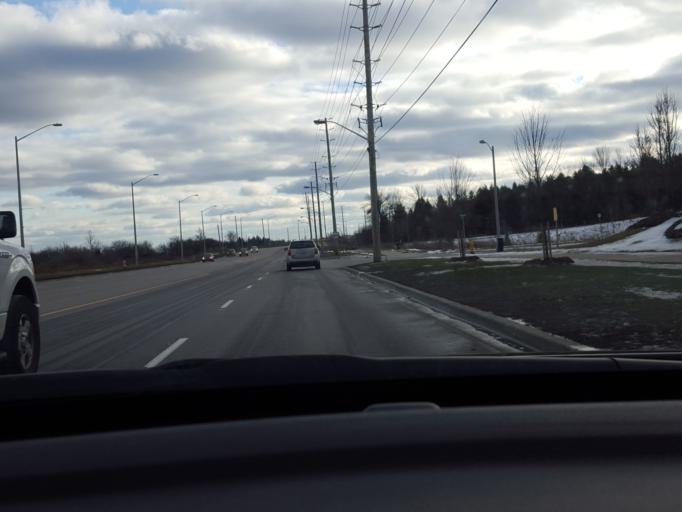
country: CA
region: Ontario
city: Ajax
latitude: 43.8782
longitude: -79.0172
